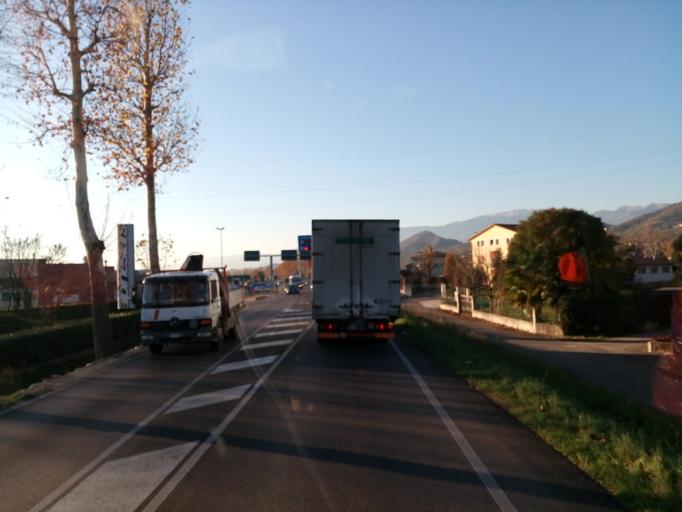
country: IT
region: Veneto
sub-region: Provincia di Treviso
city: Maser
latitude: 45.7939
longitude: 11.9670
